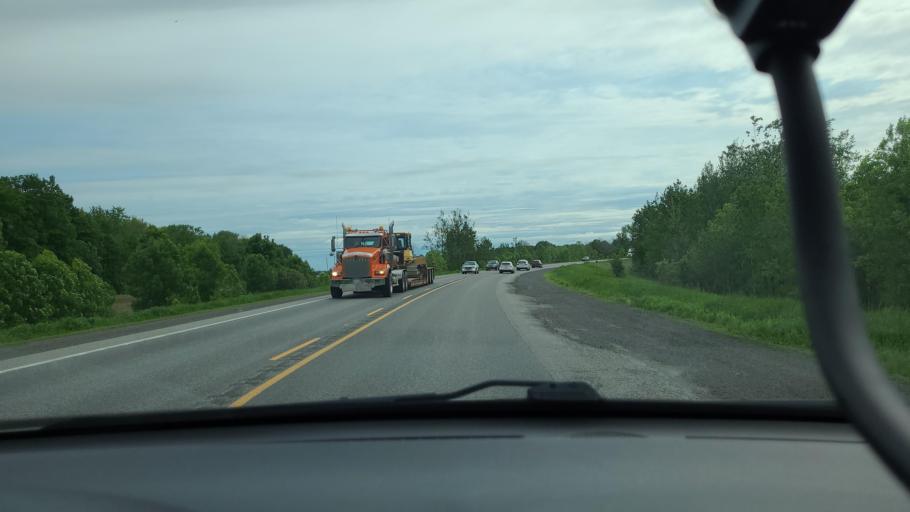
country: CA
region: Quebec
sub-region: Lanaudiere
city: Saint-Jacques
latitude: 45.9722
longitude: -73.5498
